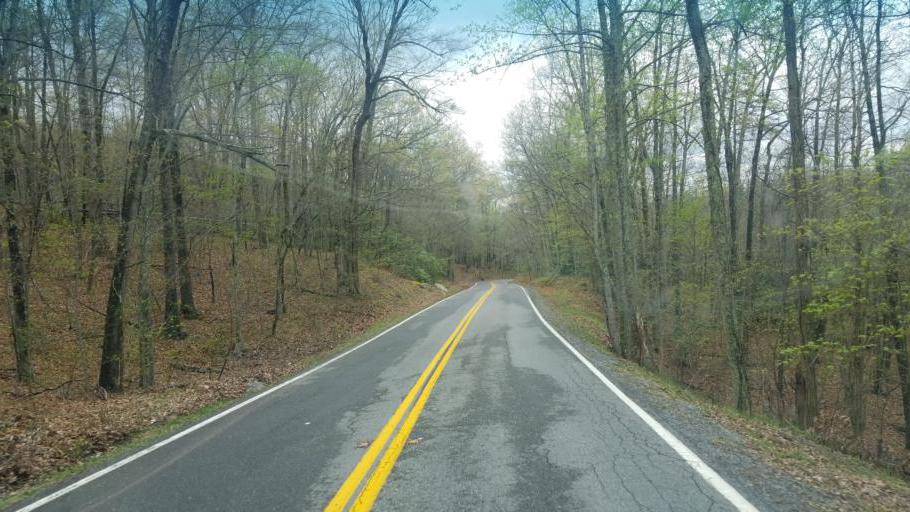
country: US
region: Virginia
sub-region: Tazewell County
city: Tazewell
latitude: 36.9941
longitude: -81.5324
